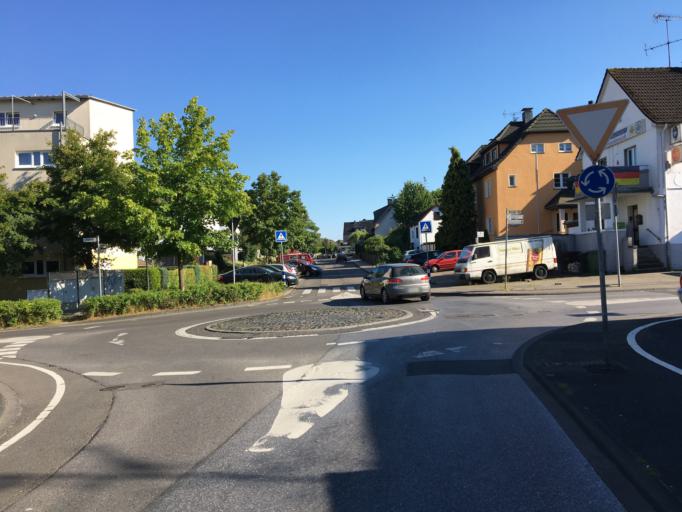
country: DE
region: North Rhine-Westphalia
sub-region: Regierungsbezirk Koln
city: Rosrath
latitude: 50.8917
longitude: 7.1801
